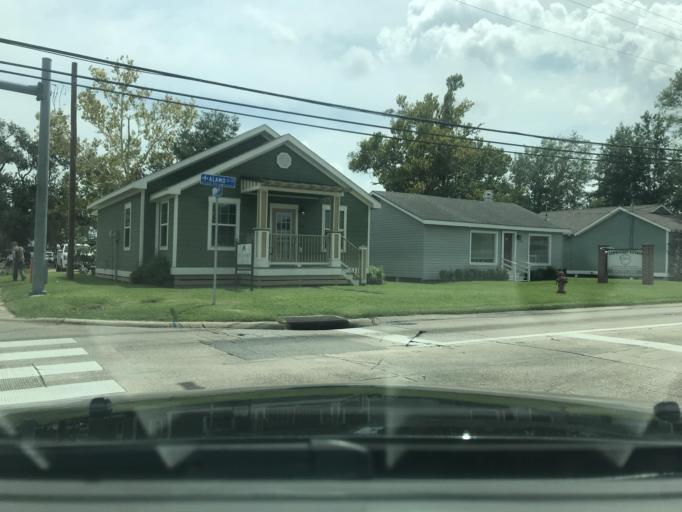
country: US
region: Louisiana
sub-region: Calcasieu Parish
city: Lake Charles
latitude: 30.2034
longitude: -93.2141
